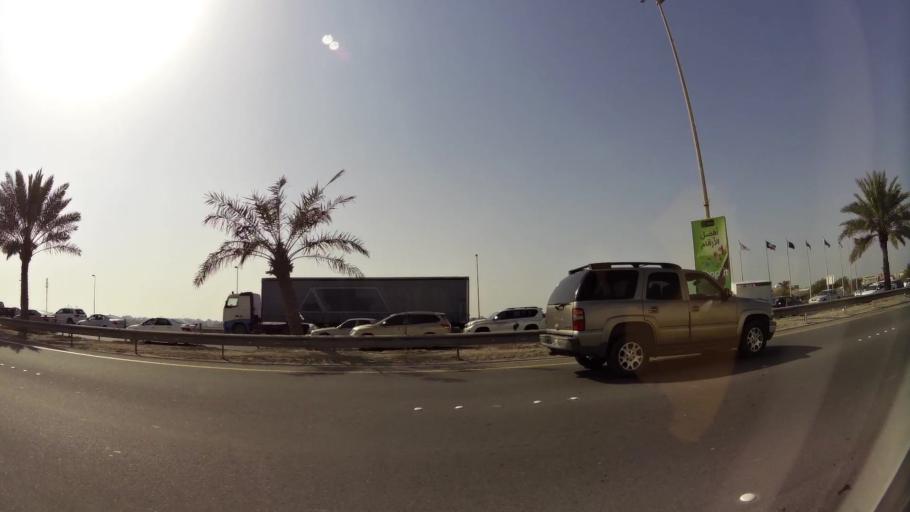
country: BH
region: Northern
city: Madinat `Isa
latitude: 26.1916
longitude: 50.5053
